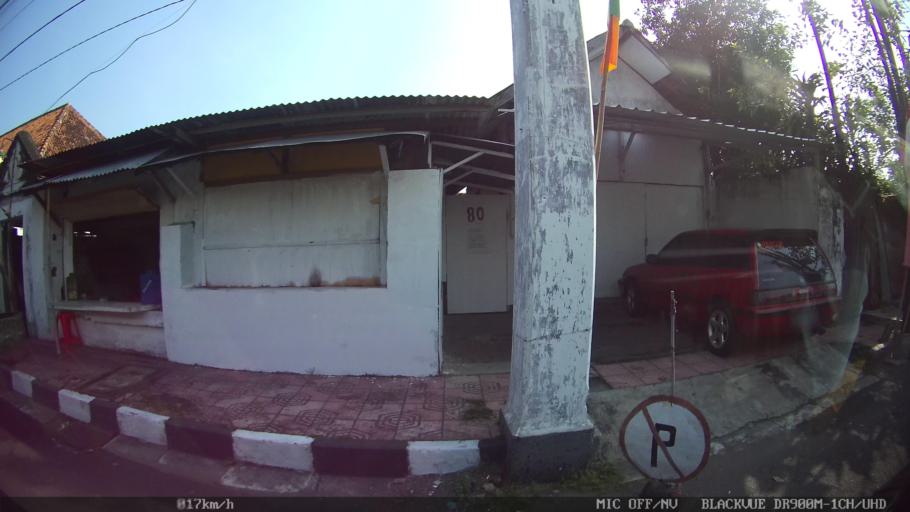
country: ID
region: Daerah Istimewa Yogyakarta
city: Yogyakarta
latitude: -7.8075
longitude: 110.3586
